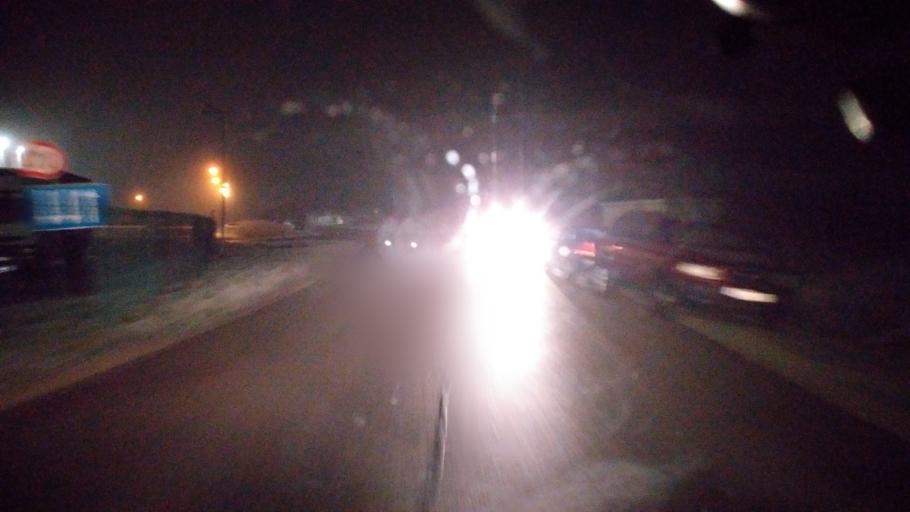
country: LV
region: Olaine
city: Olaine
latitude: 56.8001
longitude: 23.9462
